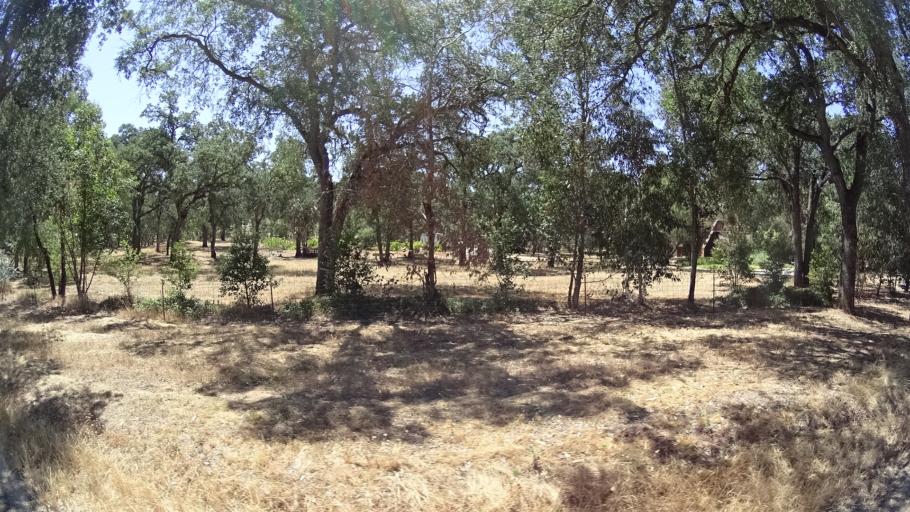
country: US
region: California
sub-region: Calaveras County
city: Rancho Calaveras
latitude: 38.1487
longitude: -120.9002
